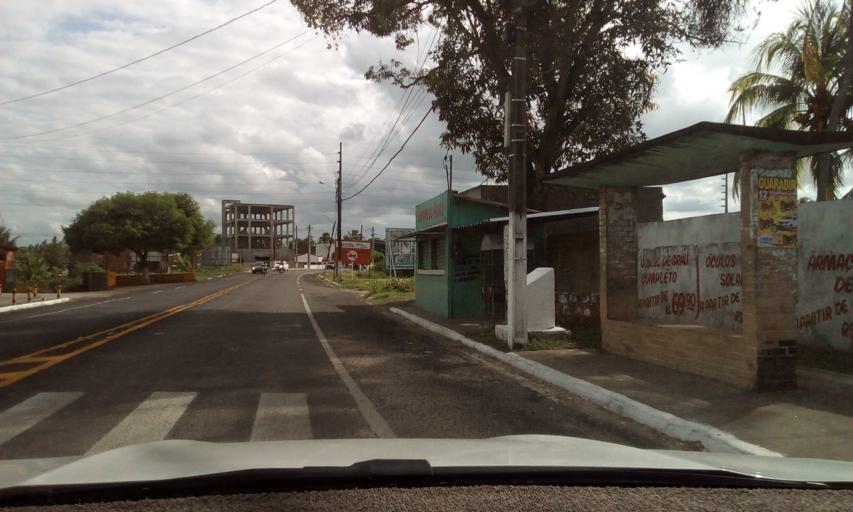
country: BR
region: Paraiba
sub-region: Rio Tinto
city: Rio Tinto
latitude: -6.8124
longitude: -35.0815
